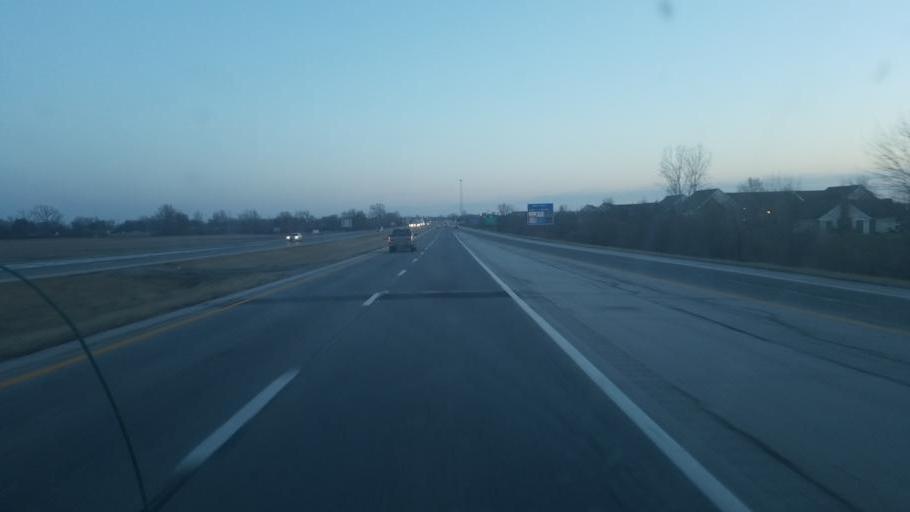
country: US
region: Ohio
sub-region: Marion County
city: Marion
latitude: 40.5927
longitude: -83.0827
